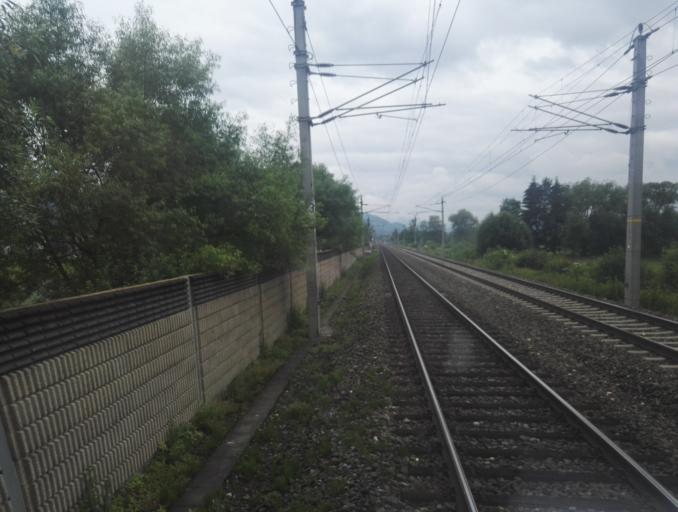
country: AT
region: Styria
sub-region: Politischer Bezirk Bruck-Muerzzuschlag
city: Allerheiligen im Muerztal
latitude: 47.4860
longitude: 15.4100
